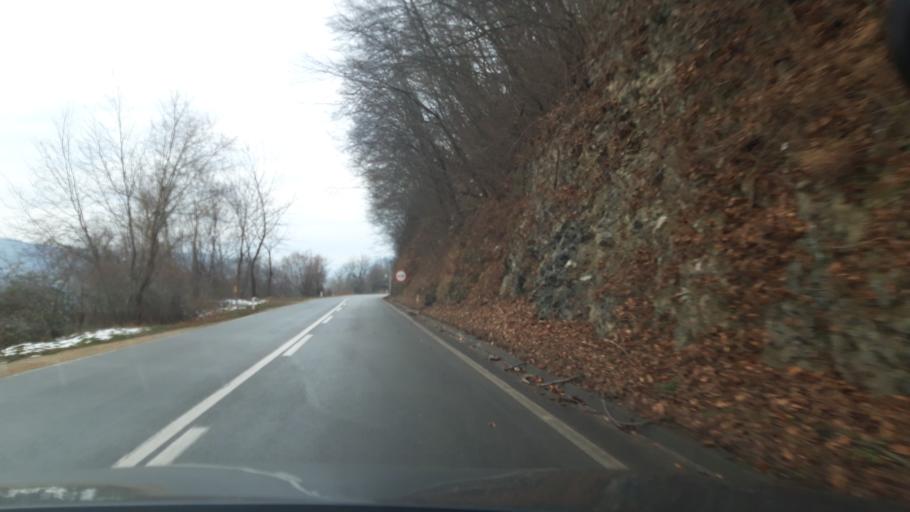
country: RS
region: Central Serbia
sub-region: Macvanski Okrug
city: Mali Zvornik
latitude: 44.3022
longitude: 19.1459
